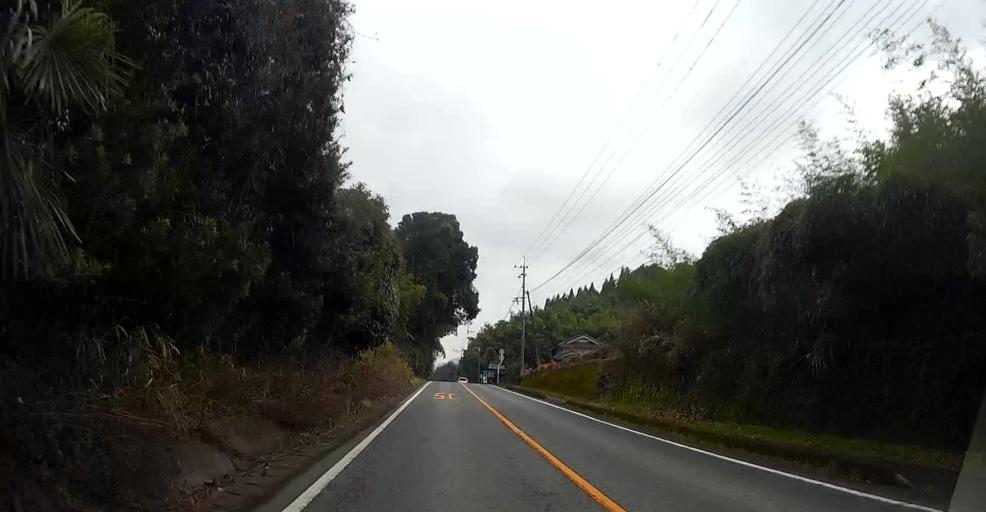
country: JP
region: Kumamoto
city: Matsubase
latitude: 32.6449
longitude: 130.7322
